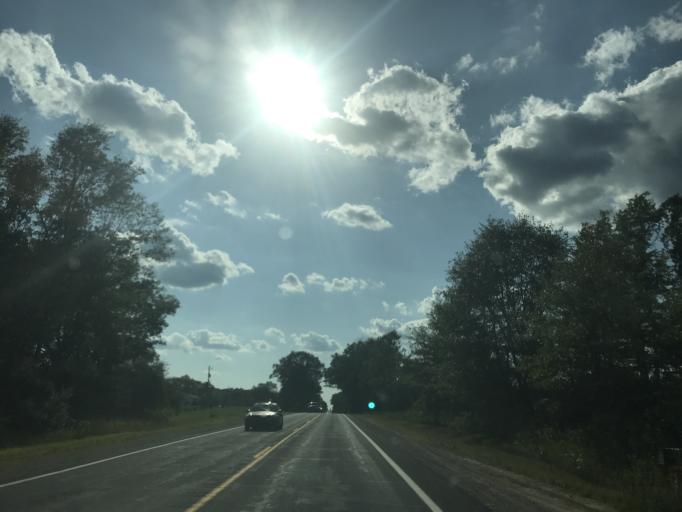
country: US
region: Michigan
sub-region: Newaygo County
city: White Cloud
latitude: 43.5685
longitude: -85.7857
